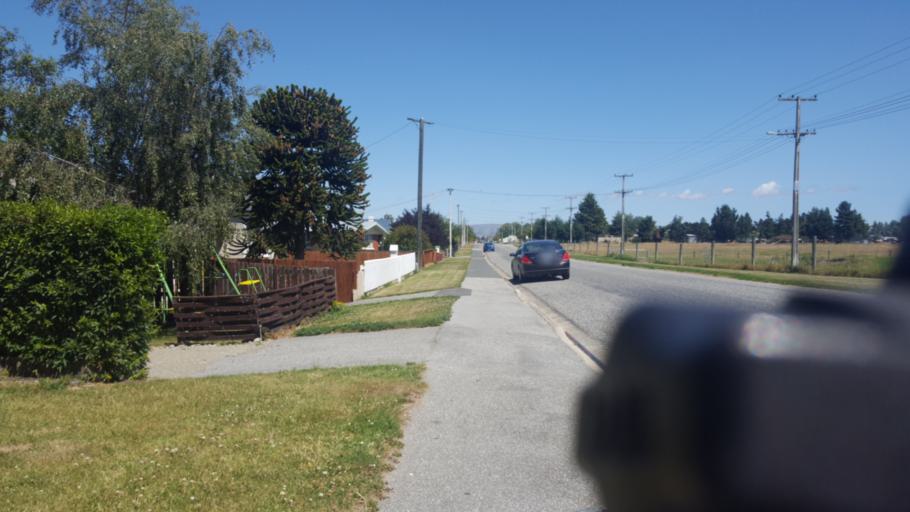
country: NZ
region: Otago
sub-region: Dunedin City
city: Dunedin
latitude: -45.1257
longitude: 170.1051
